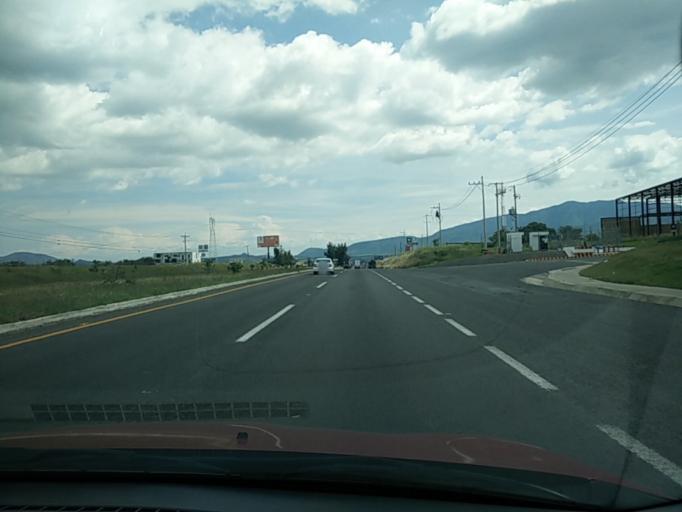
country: MX
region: Jalisco
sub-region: Ixtlahuacan de los Membrillos
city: Los Olivos
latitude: 20.4325
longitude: -103.2411
